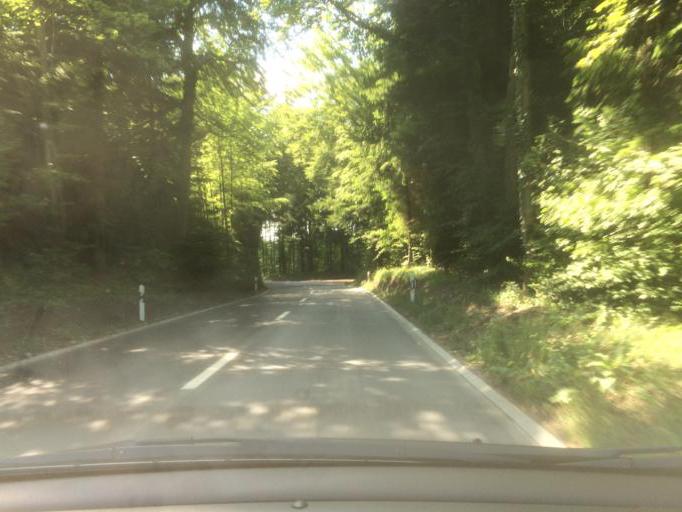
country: CH
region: Zurich
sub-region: Bezirk Uster
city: Uster / Ober-Uster
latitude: 47.3463
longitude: 8.7513
